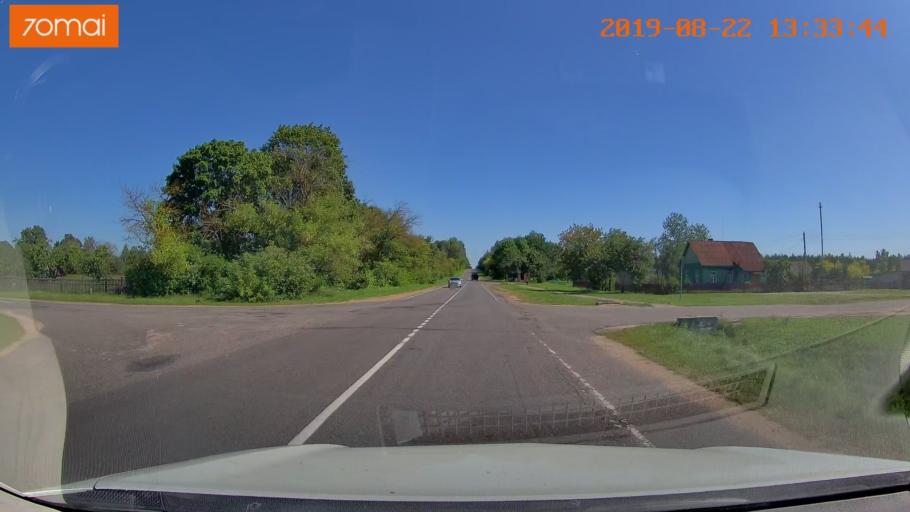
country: BY
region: Minsk
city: Staryya Darohi
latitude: 53.2161
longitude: 28.2282
